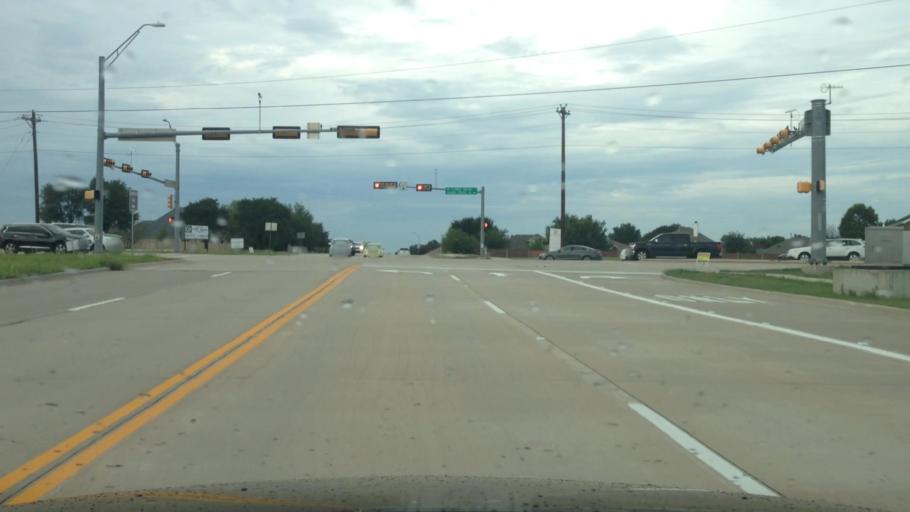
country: US
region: Texas
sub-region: Denton County
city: Lewisville
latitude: 33.0091
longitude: -97.0277
